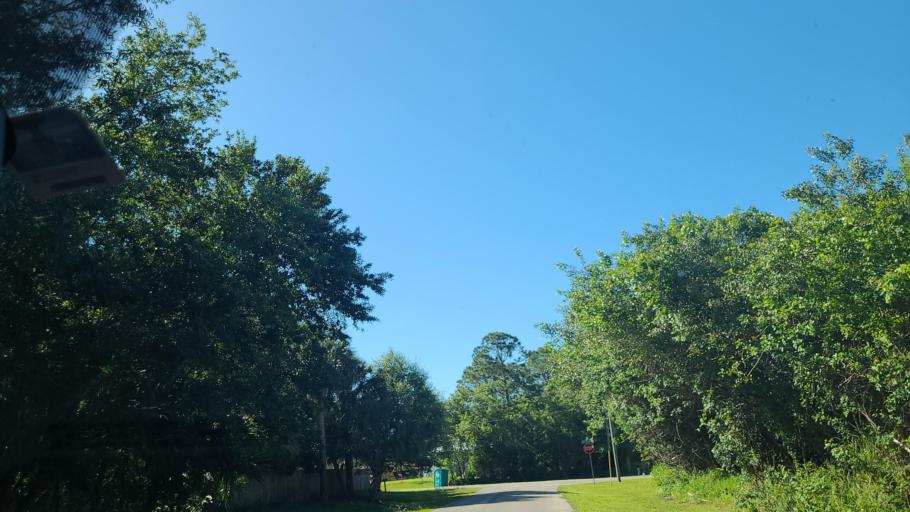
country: US
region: Florida
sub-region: Indian River County
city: Sebastian
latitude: 27.7563
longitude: -80.4868
